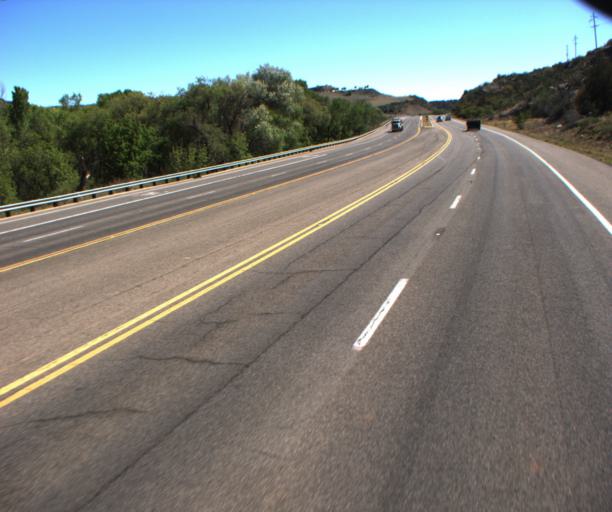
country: US
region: Arizona
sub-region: Yavapai County
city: Prescott
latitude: 34.5651
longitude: -112.4437
